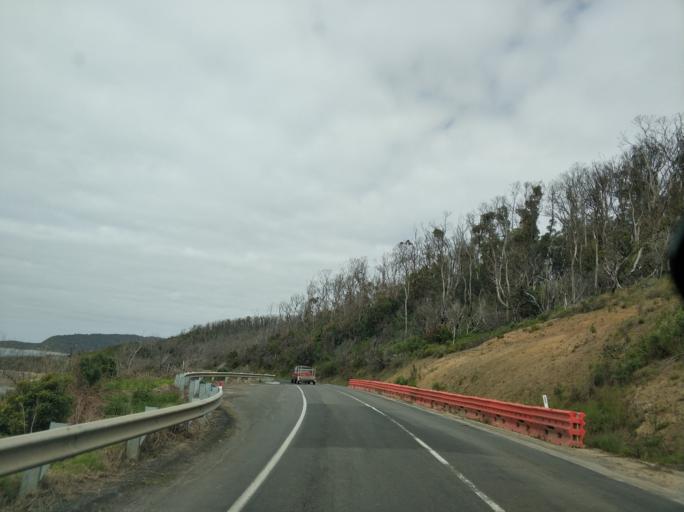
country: AU
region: Victoria
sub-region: Colac-Otway
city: Apollo Bay
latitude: -38.6426
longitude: 143.8877
